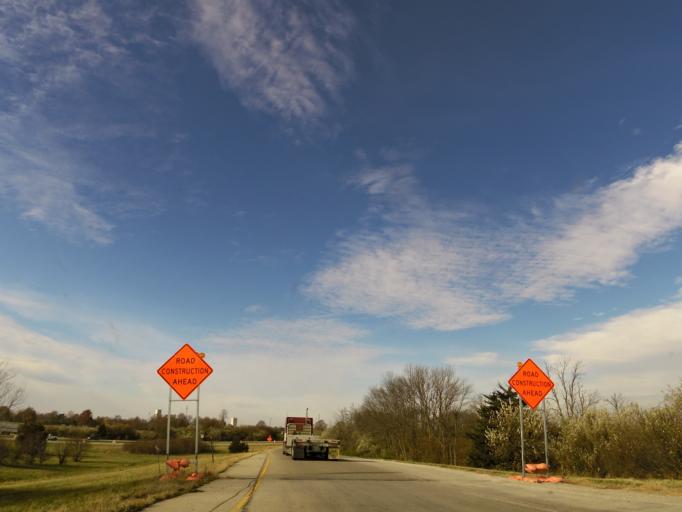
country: US
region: Illinois
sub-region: De Witt County
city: Farmer City
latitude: 40.2533
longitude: -88.6247
